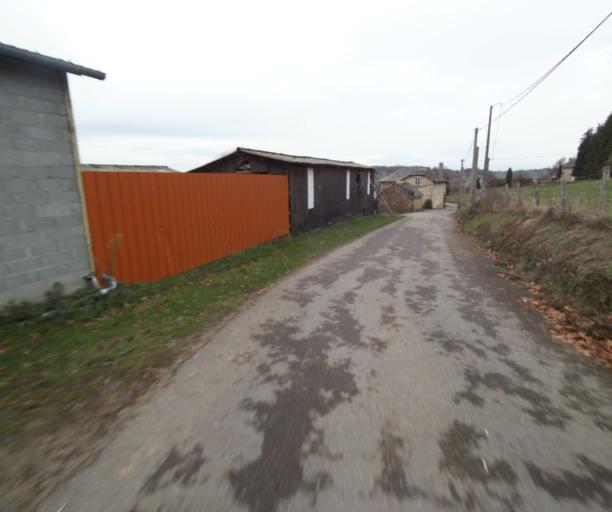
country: FR
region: Limousin
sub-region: Departement de la Correze
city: Chameyrat
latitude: 45.2349
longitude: 1.6531
